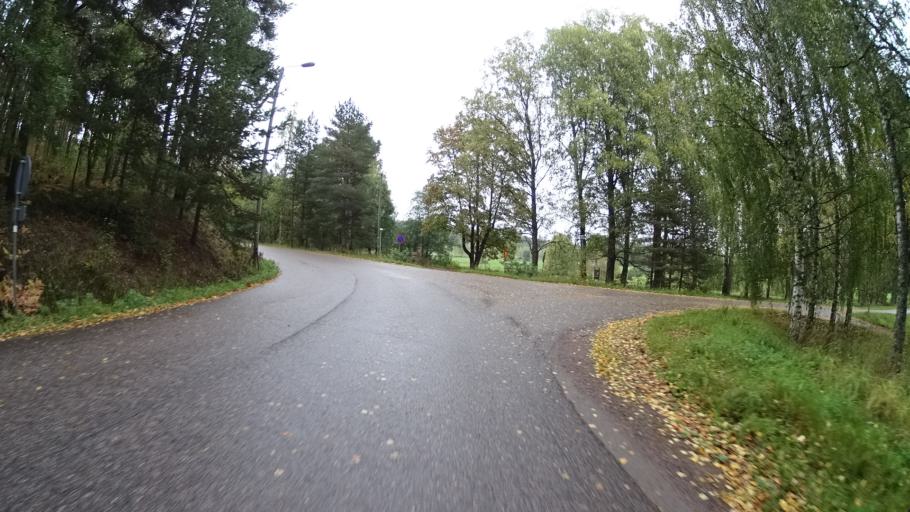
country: FI
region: Uusimaa
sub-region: Helsinki
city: Kauniainen
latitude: 60.3185
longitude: 24.6899
